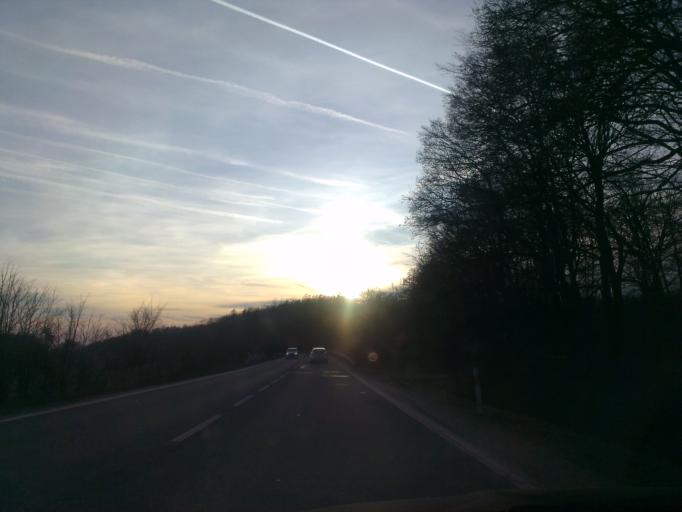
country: CZ
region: South Moravian
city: Bilovice nad Svitavou
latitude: 49.2240
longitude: 16.6868
